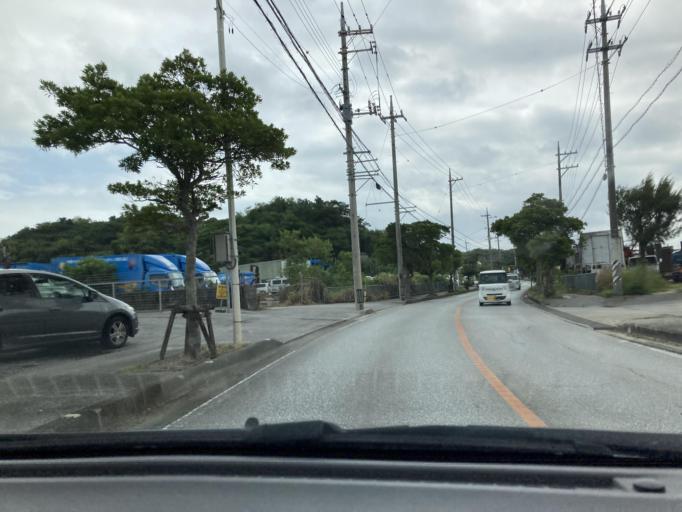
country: JP
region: Okinawa
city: Ginowan
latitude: 26.2611
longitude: 127.7769
